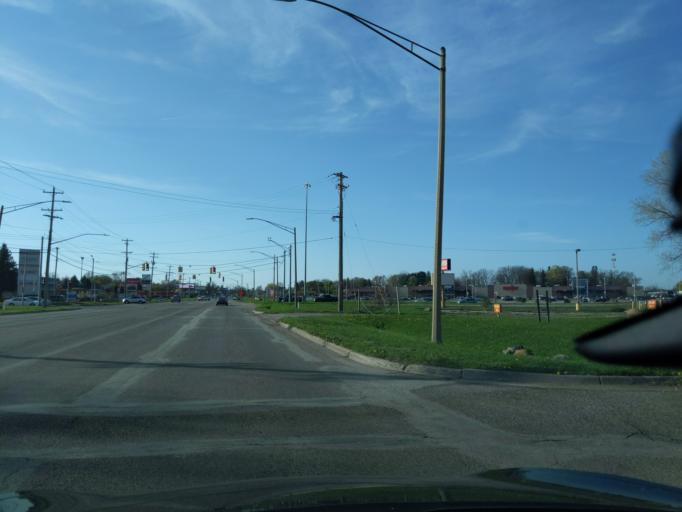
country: US
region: Michigan
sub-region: Ingham County
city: Holt
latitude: 42.6649
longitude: -84.5410
